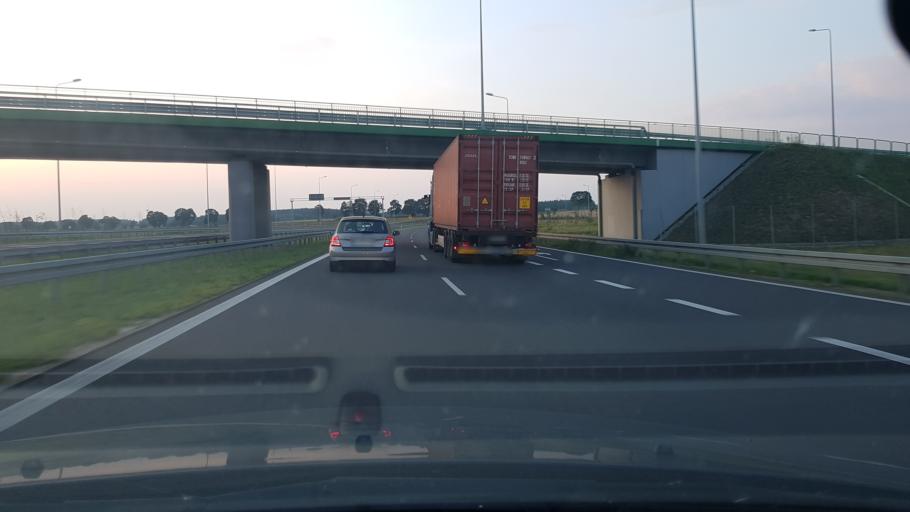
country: PL
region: Masovian Voivodeship
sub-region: Powiat mlawski
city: Wieczfnia Koscielna
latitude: 53.2273
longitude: 20.4195
